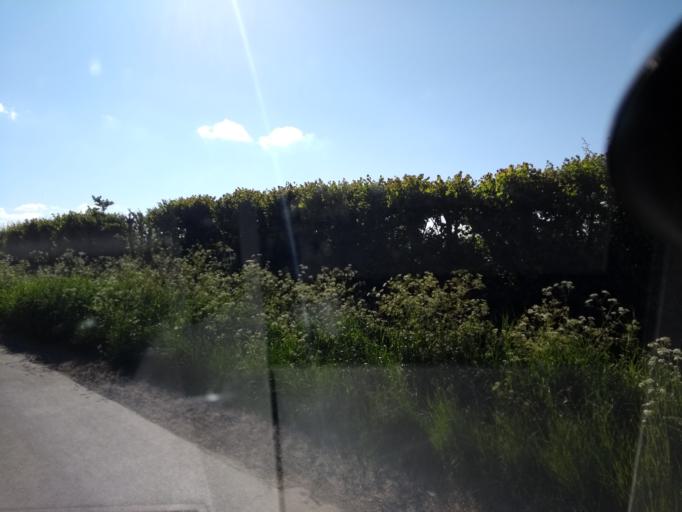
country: GB
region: England
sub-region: Somerset
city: Bridgwater
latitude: 51.1451
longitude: -3.0225
